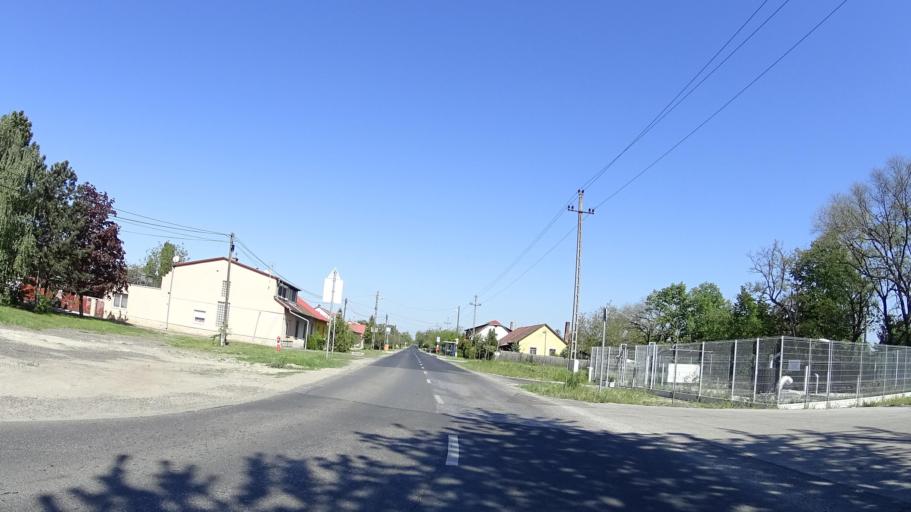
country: HU
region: Budapest
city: Budapest XXIII. keruelet
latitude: 47.3888
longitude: 19.1622
